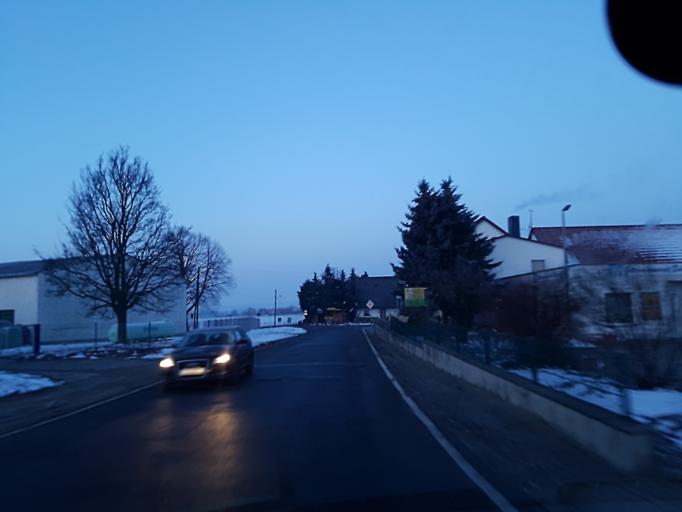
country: DE
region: Saxony
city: Oschatz
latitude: 51.3341
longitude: 13.1302
